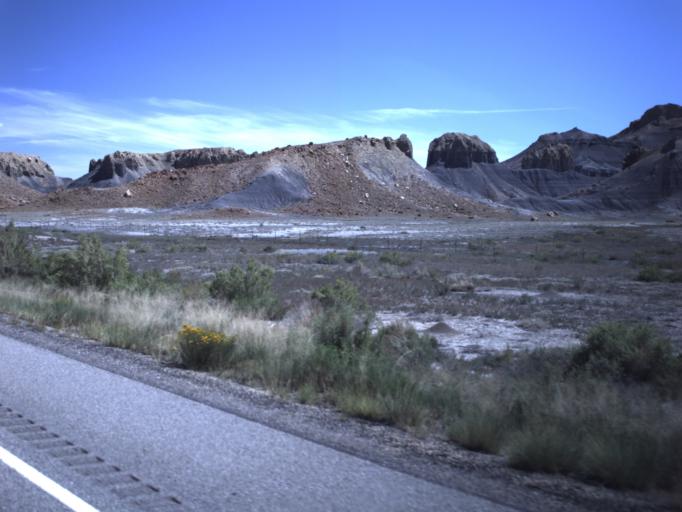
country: US
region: Utah
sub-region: Emery County
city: Ferron
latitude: 38.8096
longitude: -111.2256
